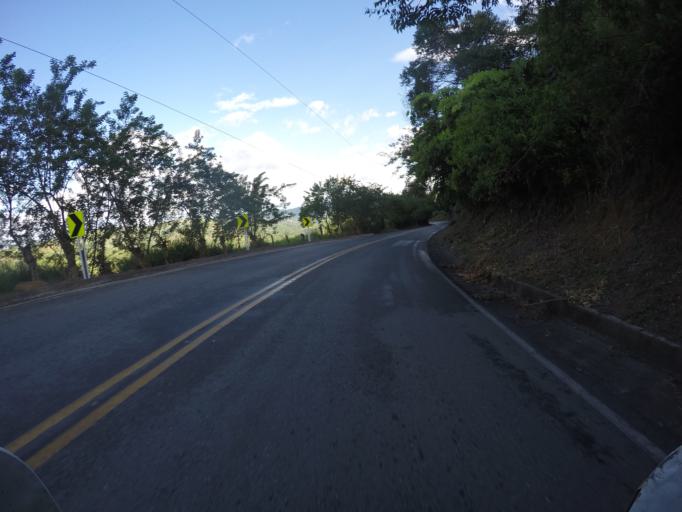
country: CO
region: Valle del Cauca
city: Cartago
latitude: 4.7257
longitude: -75.8608
